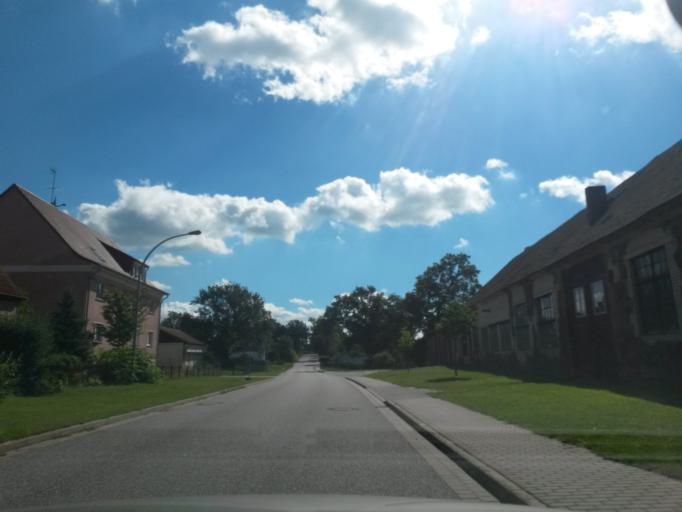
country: DE
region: Brandenburg
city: Schoneberg
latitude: 52.9995
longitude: 14.0814
